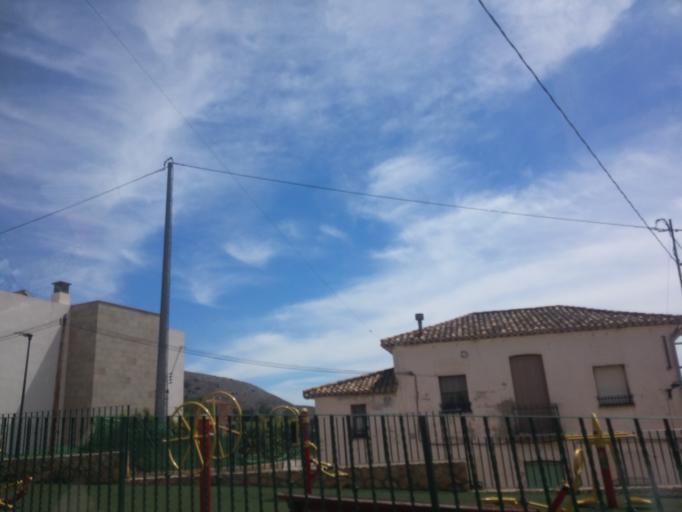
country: ES
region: Valencia
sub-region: Provincia de Alicante
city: Finestrat
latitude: 38.5693
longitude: -0.2096
